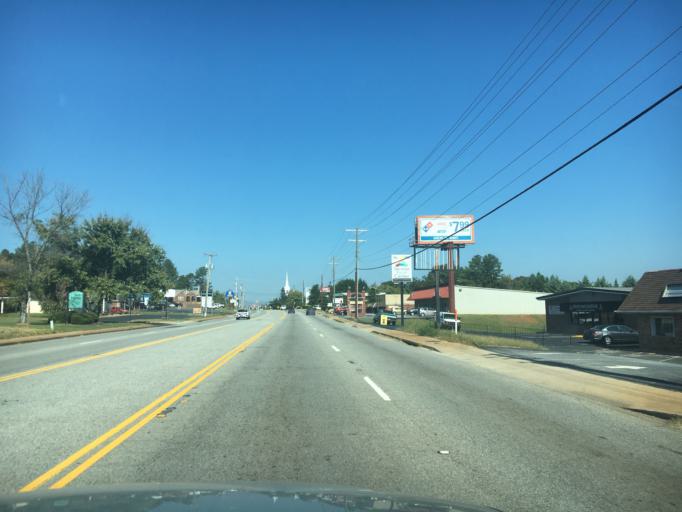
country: US
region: South Carolina
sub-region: Spartanburg County
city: Boiling Springs
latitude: 35.0407
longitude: -81.9760
